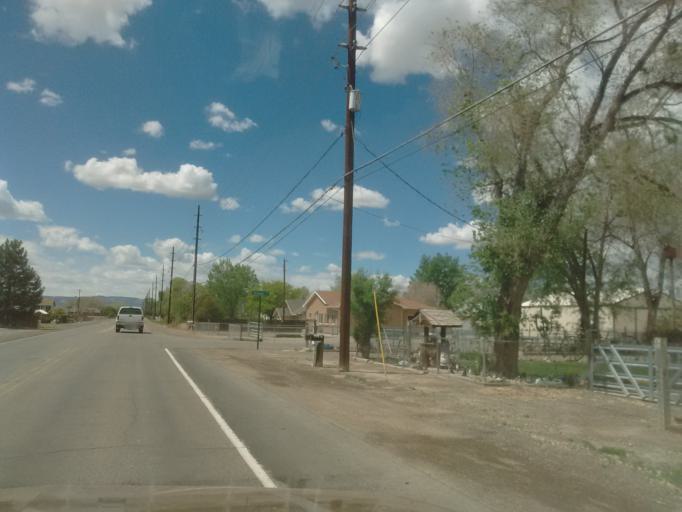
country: US
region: Colorado
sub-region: Mesa County
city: Clifton
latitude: 39.0773
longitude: -108.4619
